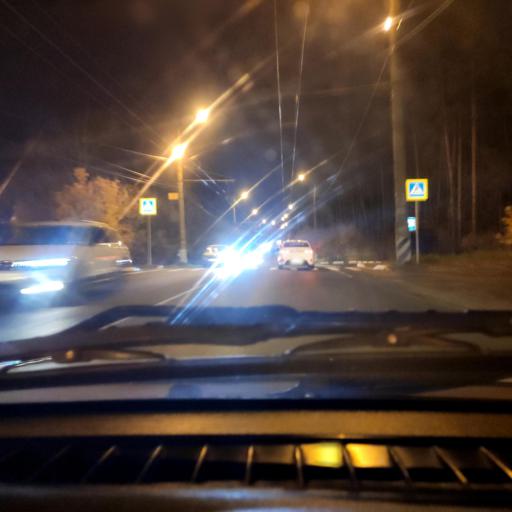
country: RU
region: Samara
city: Tol'yatti
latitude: 53.4791
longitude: 49.3521
